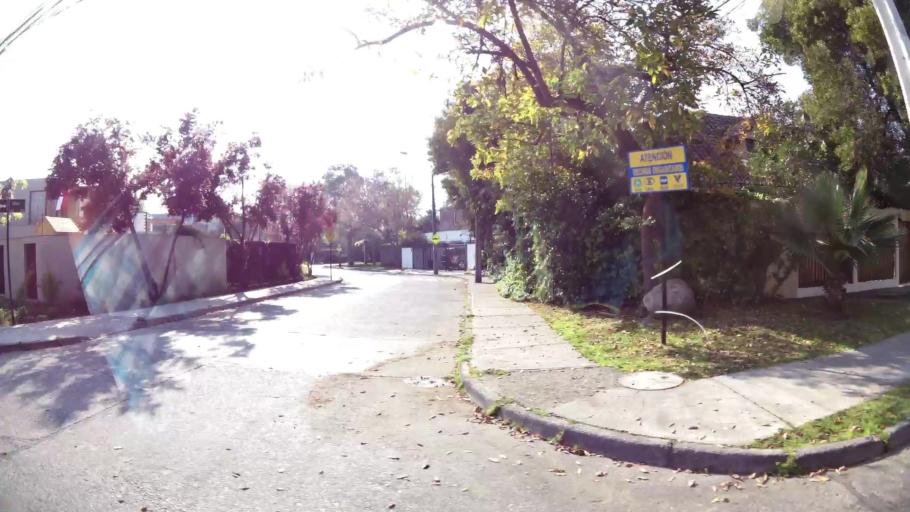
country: CL
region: Santiago Metropolitan
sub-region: Provincia de Santiago
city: Villa Presidente Frei, Nunoa, Santiago, Chile
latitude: -33.3837
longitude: -70.5653
